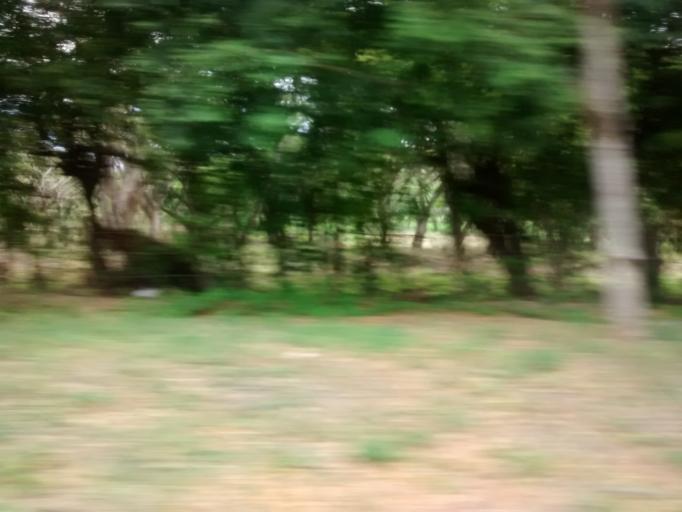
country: CO
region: Cundinamarca
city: Ricaurte
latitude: 4.2497
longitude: -74.7289
